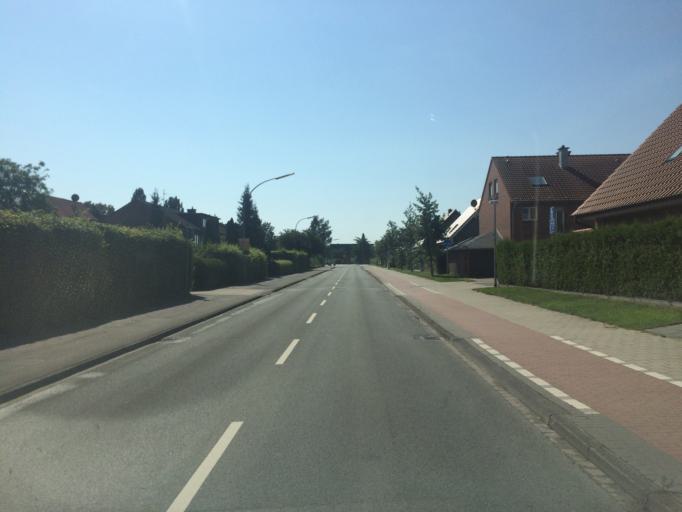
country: DE
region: North Rhine-Westphalia
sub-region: Regierungsbezirk Munster
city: Telgte
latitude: 52.0008
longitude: 7.7098
